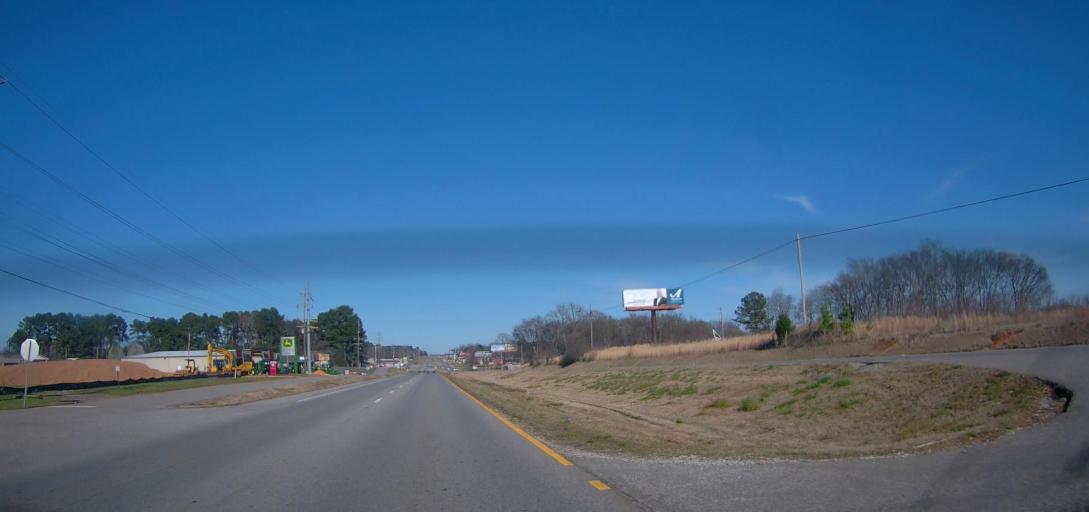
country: US
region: Alabama
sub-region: Lauderdale County
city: East Florence
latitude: 34.8391
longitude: -87.6000
